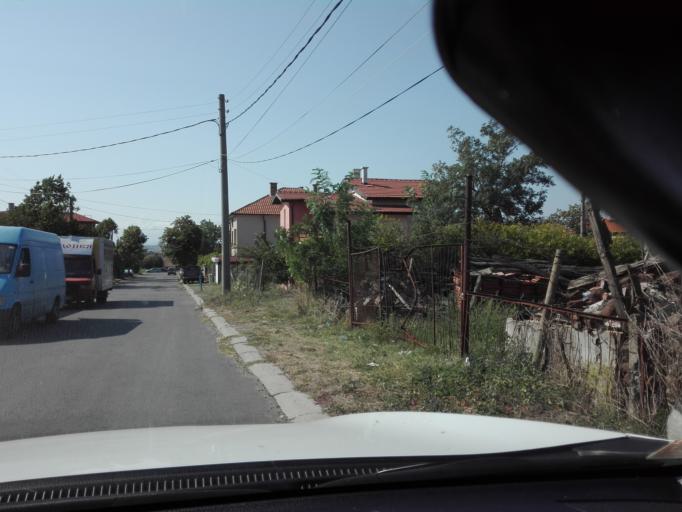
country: BG
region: Burgas
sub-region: Obshtina Kameno
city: Kameno
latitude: 42.6296
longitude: 27.3950
